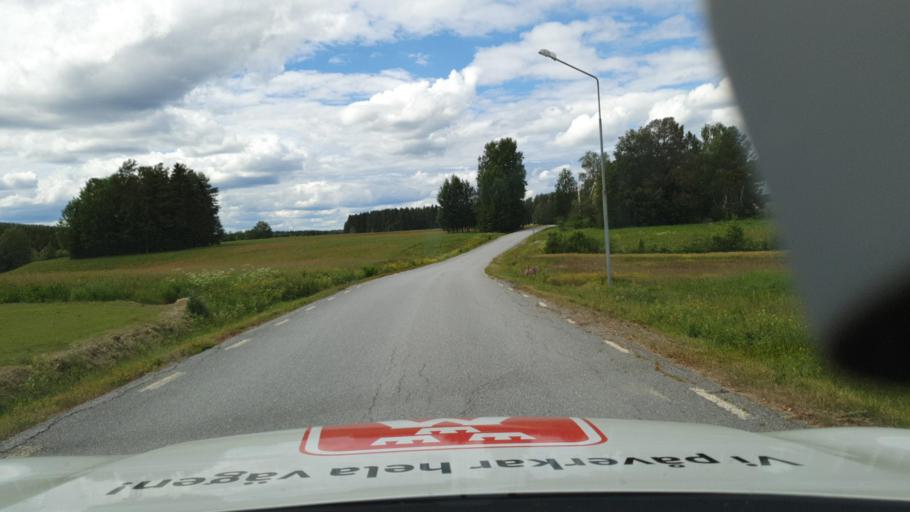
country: SE
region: Vaesterbotten
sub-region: Bjurholms Kommun
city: Bjurholm
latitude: 63.9140
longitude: 19.0790
